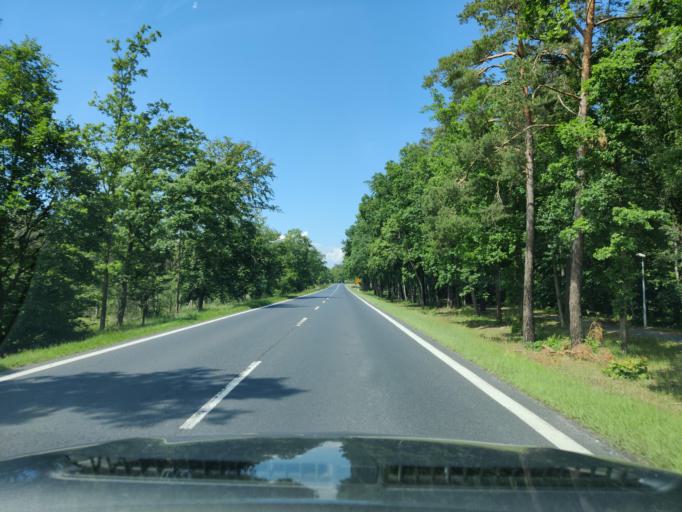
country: PL
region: Greater Poland Voivodeship
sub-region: Powiat grodziski
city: Rakoniewice
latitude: 52.1347
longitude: 16.2378
